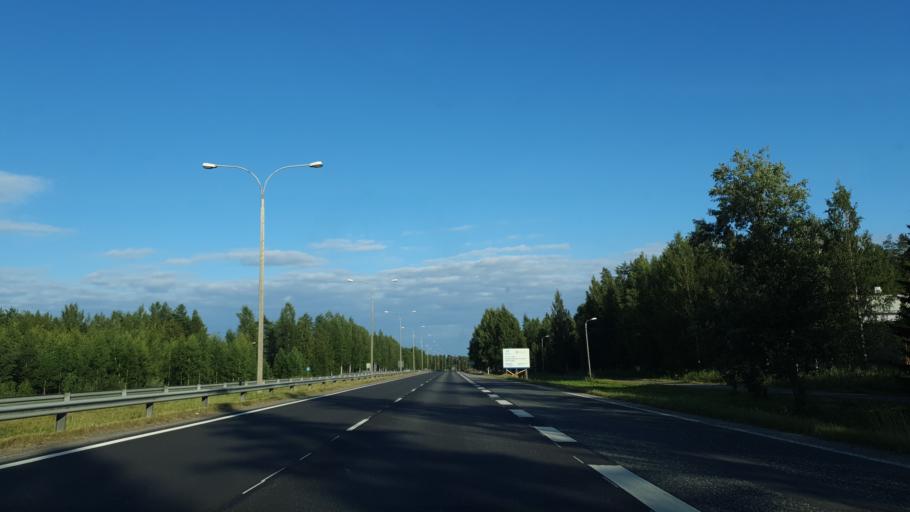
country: FI
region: North Karelia
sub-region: Joensuu
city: Joensuu
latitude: 62.6264
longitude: 29.7053
